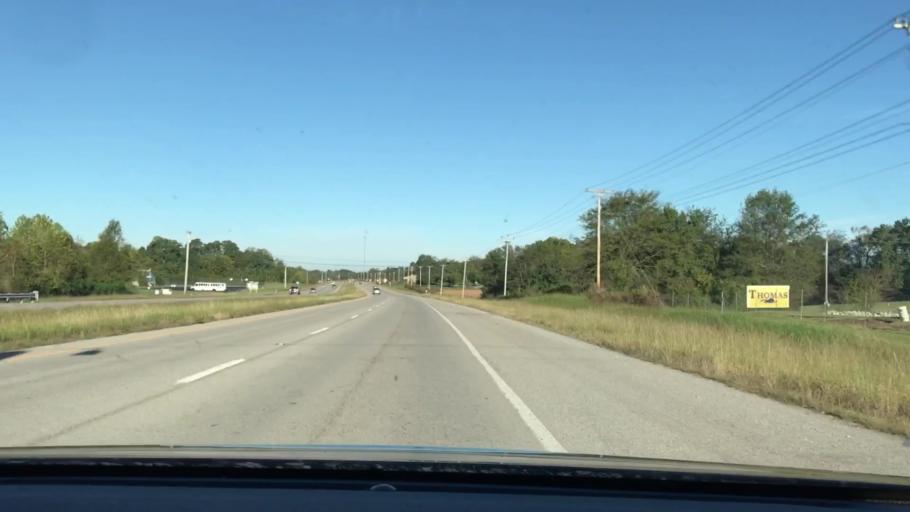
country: US
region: Kentucky
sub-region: Christian County
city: Hopkinsville
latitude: 36.8251
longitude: -87.5094
